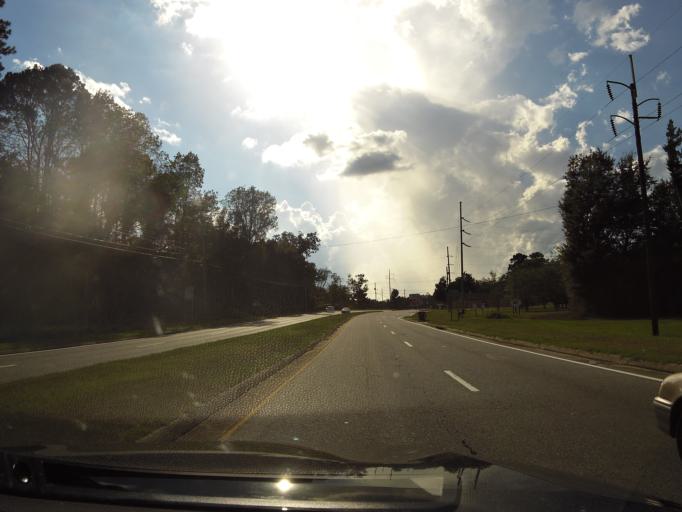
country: US
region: Georgia
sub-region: Brooks County
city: Quitman
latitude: 30.7847
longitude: -83.5424
